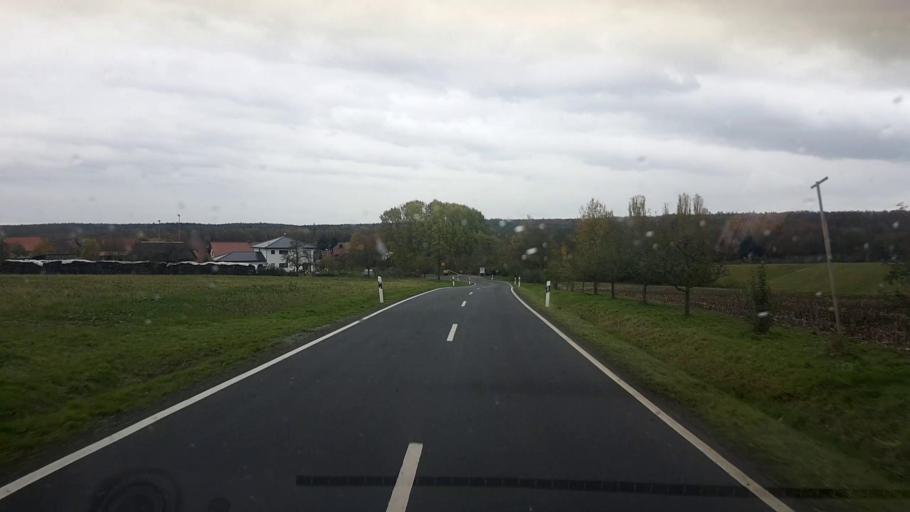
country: DE
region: Bavaria
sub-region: Upper Franconia
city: Burgwindheim
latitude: 49.8765
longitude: 10.5569
